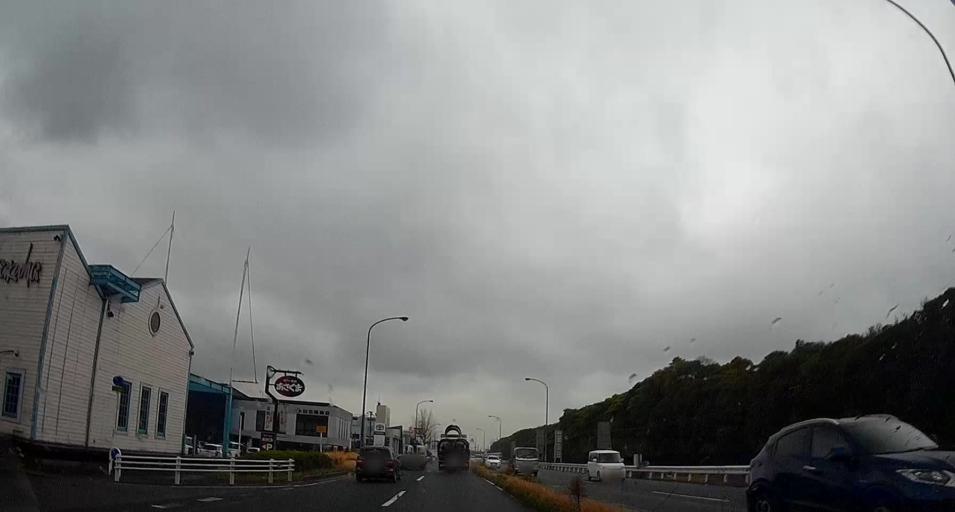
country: JP
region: Chiba
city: Ichihara
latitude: 35.5345
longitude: 140.1082
